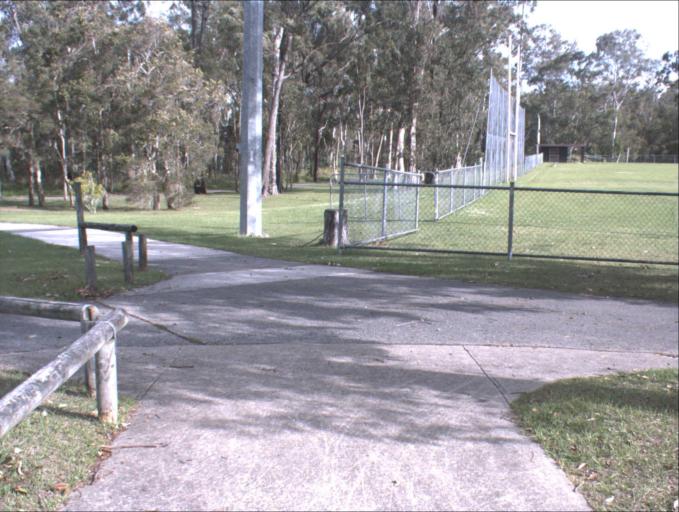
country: AU
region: Queensland
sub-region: Logan
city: Park Ridge South
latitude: -27.6713
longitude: 153.0440
